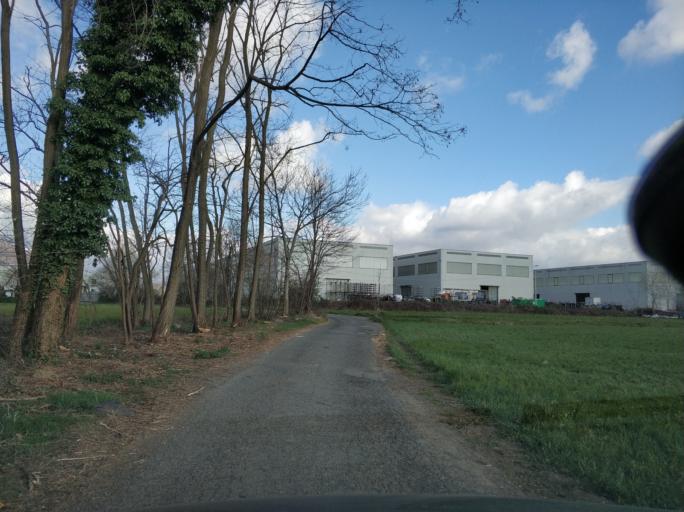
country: IT
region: Piedmont
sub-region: Provincia di Torino
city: Villanova Canavese
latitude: 45.2349
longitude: 7.5351
